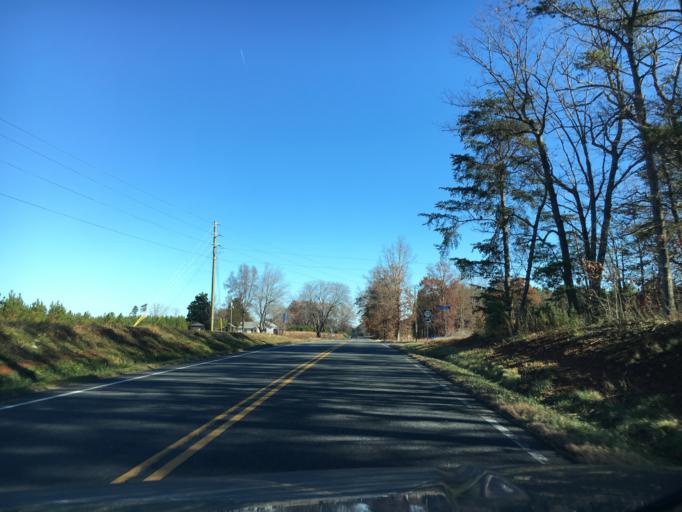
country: US
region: Virginia
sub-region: Buckingham County
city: Buckingham
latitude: 37.4858
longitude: -78.6434
